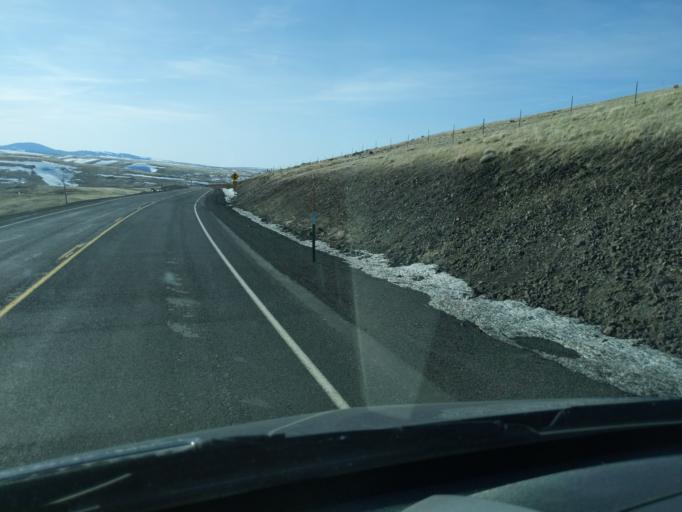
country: US
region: Oregon
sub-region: Umatilla County
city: Pilot Rock
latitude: 45.3000
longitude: -119.0000
